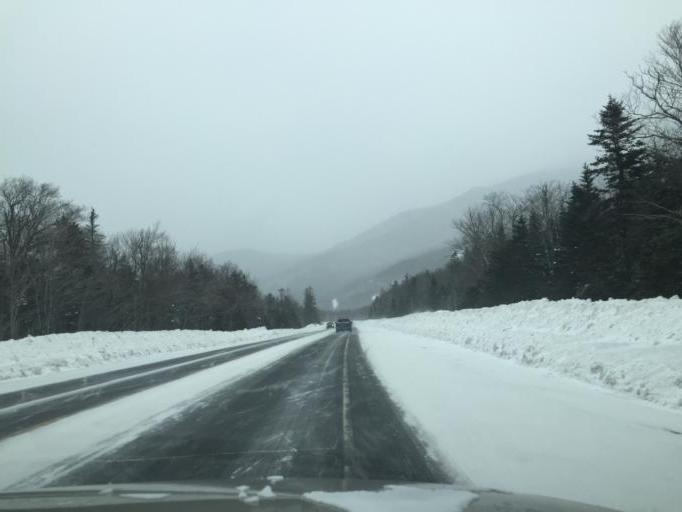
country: US
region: New Hampshire
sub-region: Coos County
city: Gorham
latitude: 44.2609
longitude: -71.2491
